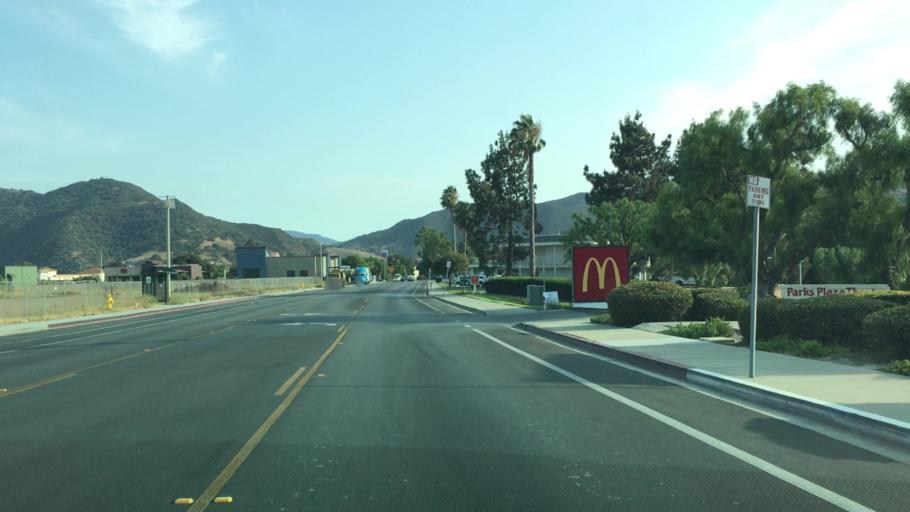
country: US
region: California
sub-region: Santa Barbara County
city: Buellton
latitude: 34.6143
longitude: -120.1882
